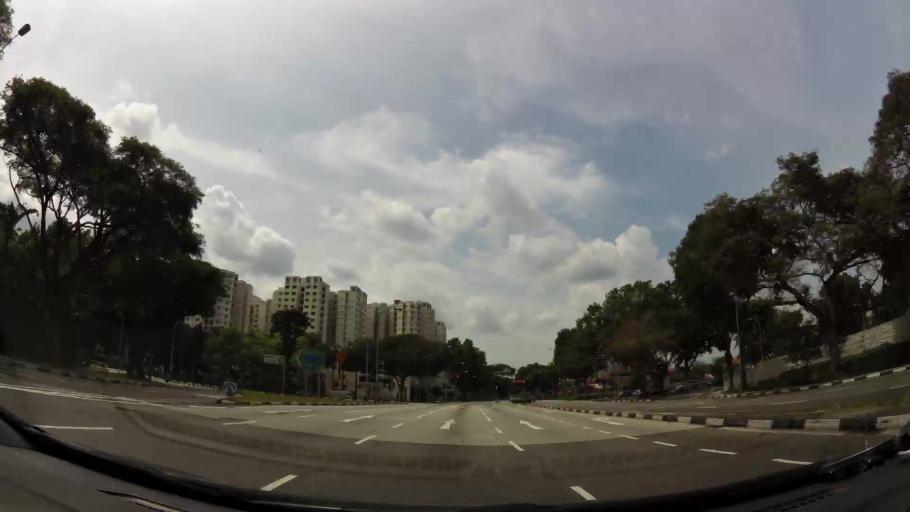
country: MY
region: Johor
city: Johor Bahru
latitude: 1.3474
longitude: 103.7057
